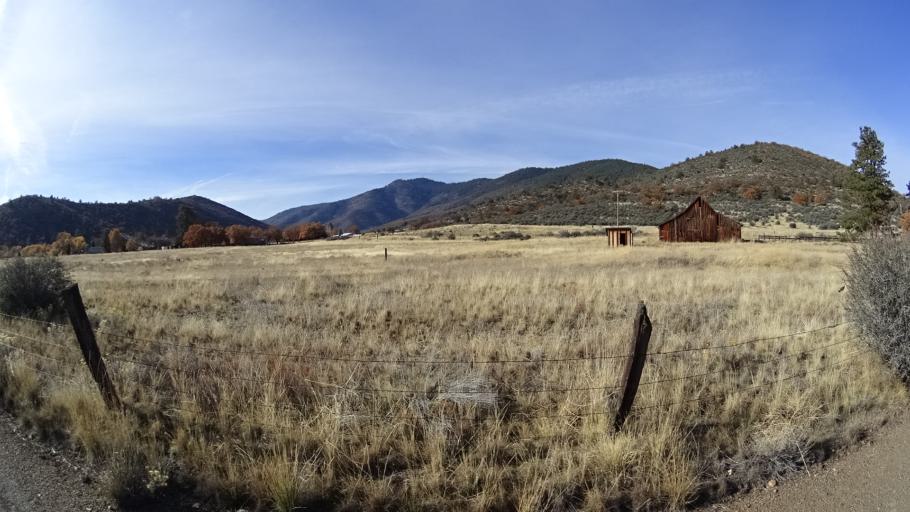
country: US
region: California
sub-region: Siskiyou County
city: Montague
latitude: 41.6384
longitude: -122.5732
